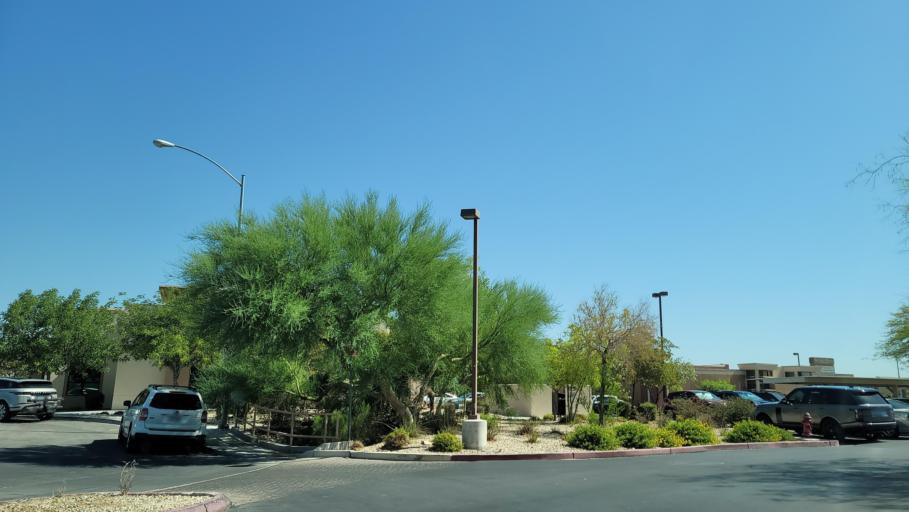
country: US
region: Nevada
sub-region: Clark County
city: Spring Valley
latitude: 36.0737
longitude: -115.2907
